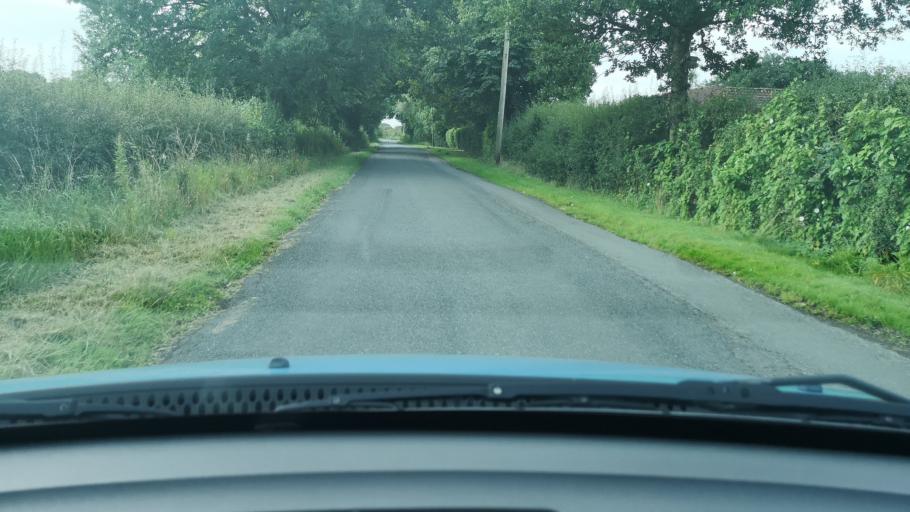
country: GB
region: England
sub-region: Doncaster
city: Stainforth
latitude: 53.6447
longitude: -1.0349
